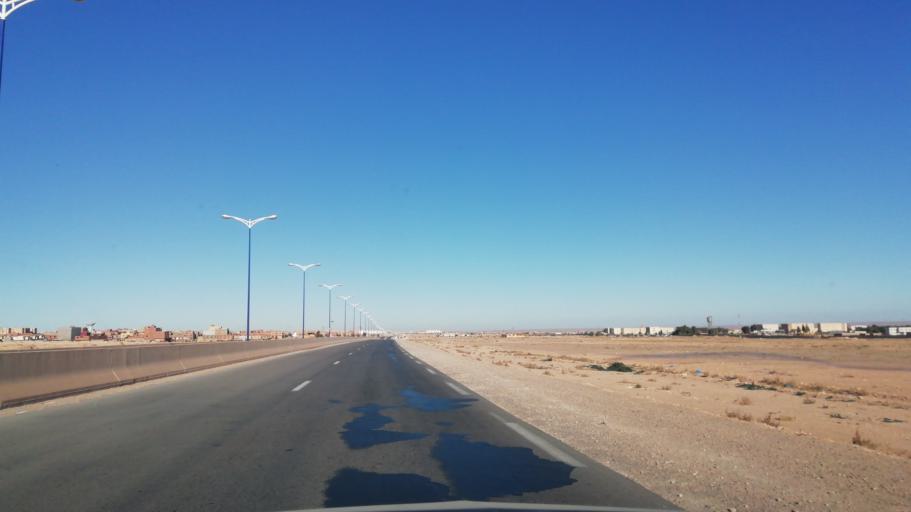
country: DZ
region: Wilaya de Naama
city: Naama
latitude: 33.5304
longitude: -0.2713
